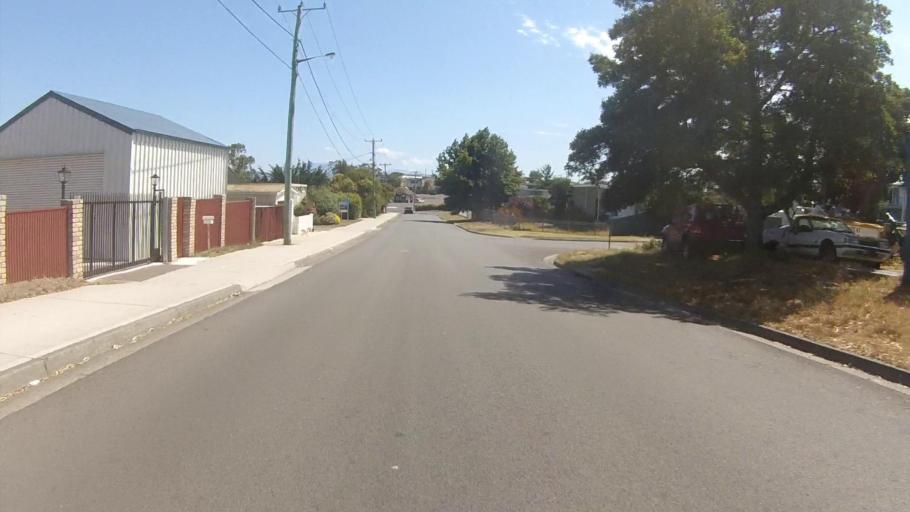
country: AU
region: Tasmania
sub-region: Sorell
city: Sorell
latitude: -42.8028
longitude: 147.5341
